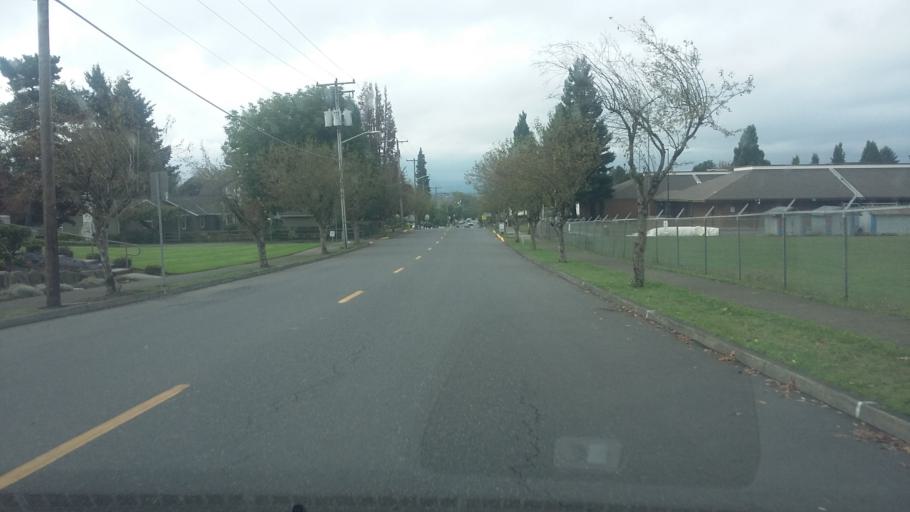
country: US
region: Washington
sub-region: Clark County
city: Ridgefield
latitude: 45.8154
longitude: -122.7403
